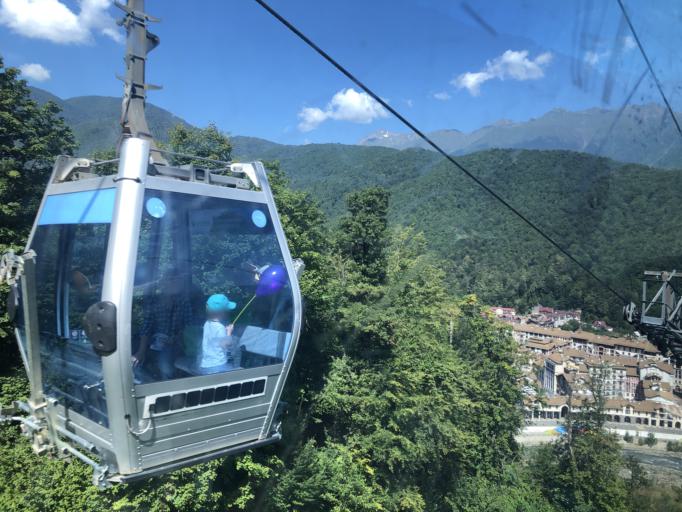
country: RU
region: Krasnodarskiy
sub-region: Sochi City
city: Krasnaya Polyana
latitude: 43.6794
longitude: 40.2648
